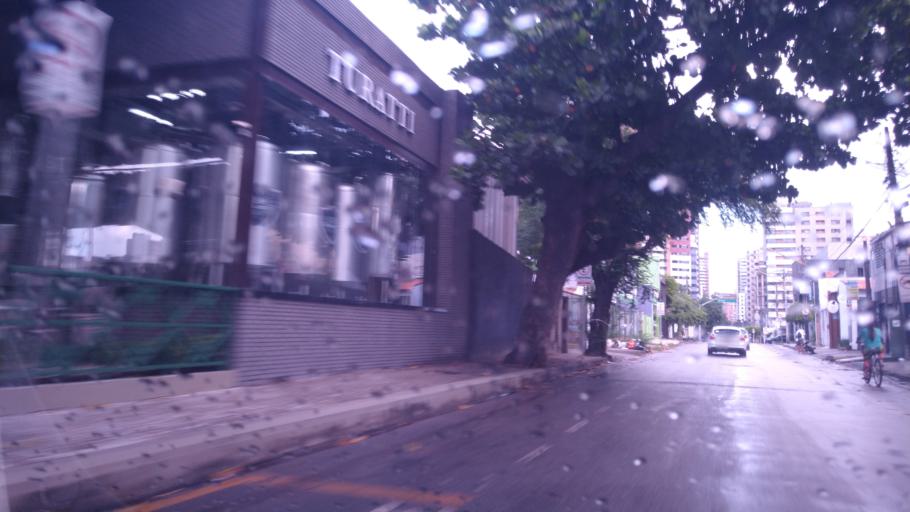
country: BR
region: Ceara
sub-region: Fortaleza
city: Fortaleza
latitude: -3.7315
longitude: -38.4895
